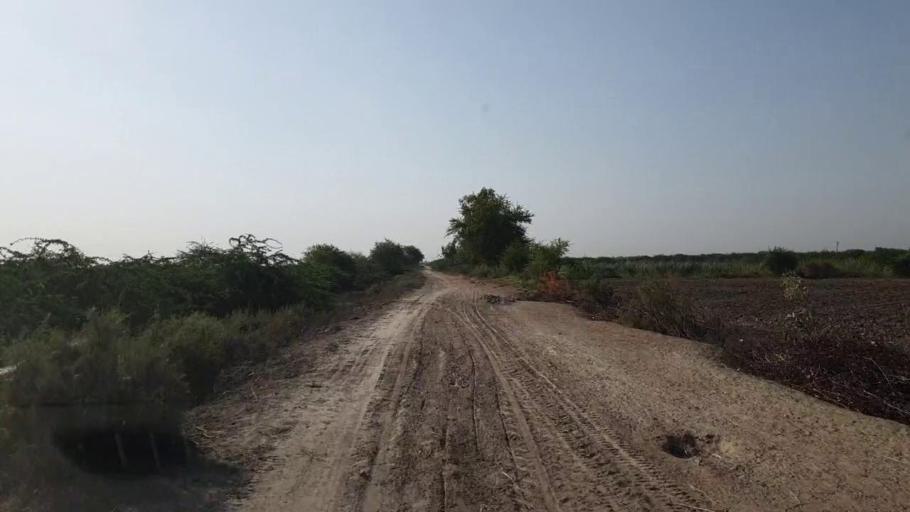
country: PK
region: Sindh
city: Kadhan
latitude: 24.6167
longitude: 69.0730
